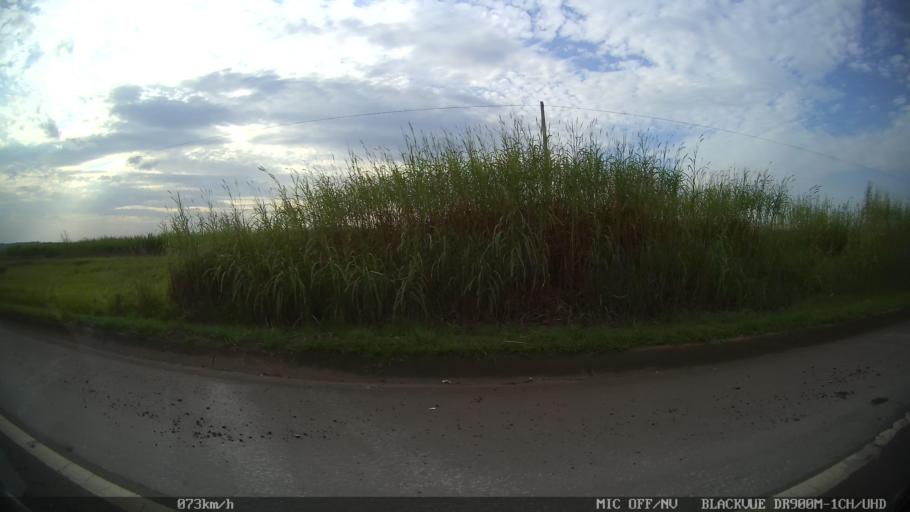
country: BR
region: Sao Paulo
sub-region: Cosmopolis
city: Cosmopolis
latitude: -22.6269
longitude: -47.2658
